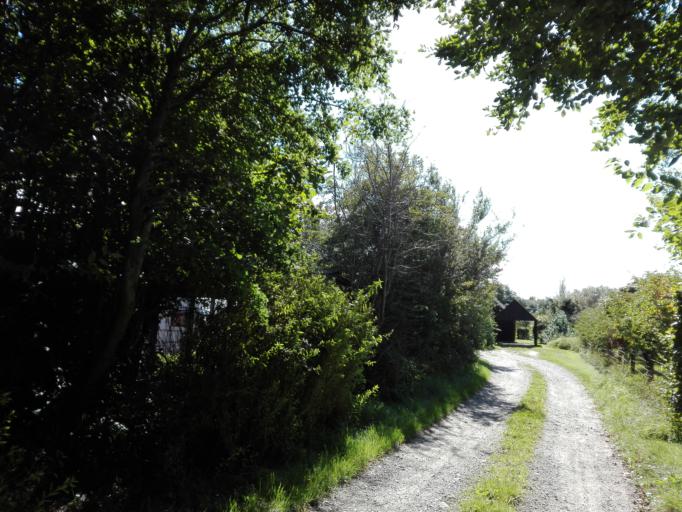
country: DK
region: Central Jutland
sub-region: Arhus Kommune
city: Beder
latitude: 56.0594
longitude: 10.2224
